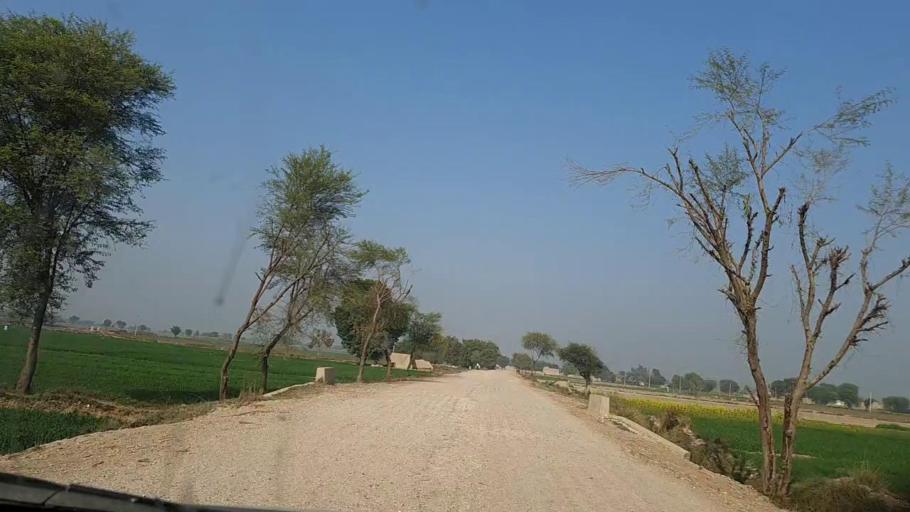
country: PK
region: Sindh
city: Moro
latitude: 26.7744
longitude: 67.9332
